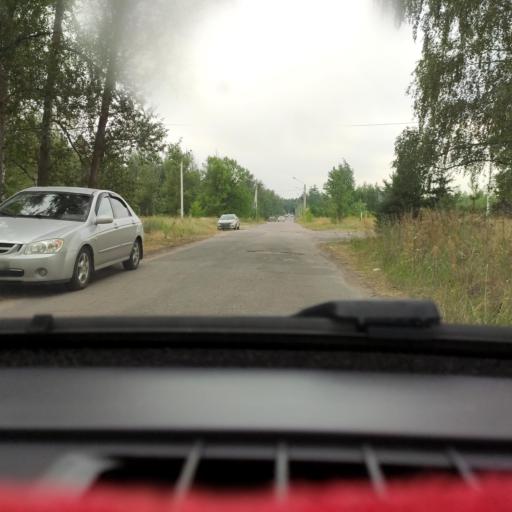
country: RU
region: Voronezj
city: Somovo
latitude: 51.7321
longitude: 39.3196
